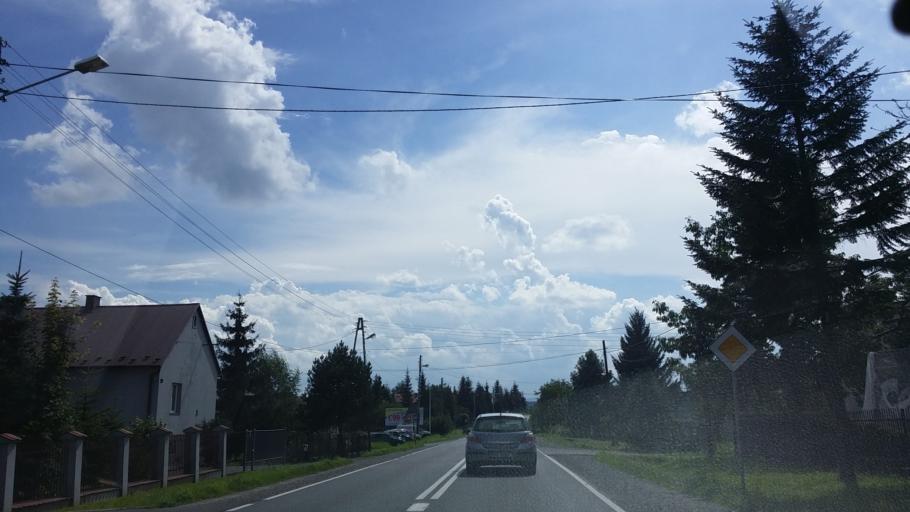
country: PL
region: Lesser Poland Voivodeship
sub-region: Powiat wielicki
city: Pawlikowice
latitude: 49.9625
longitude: 20.0562
